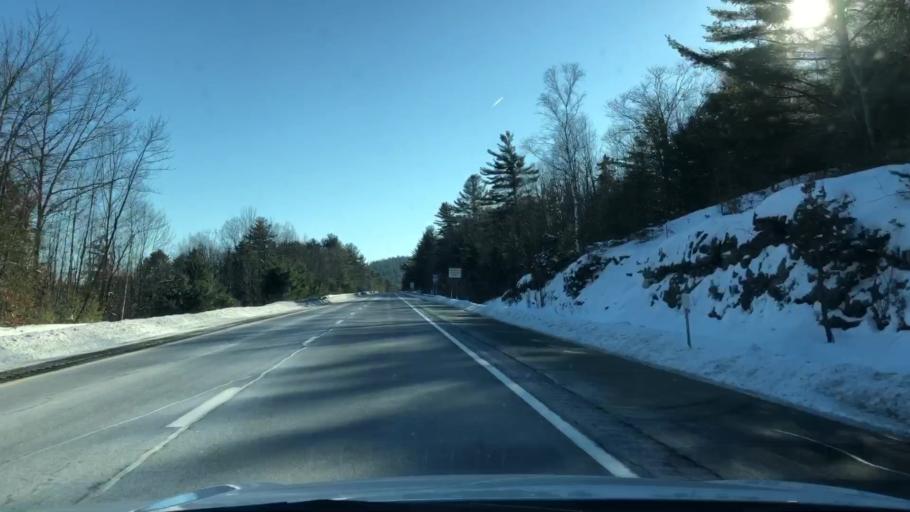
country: US
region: New York
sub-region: Warren County
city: Warrensburg
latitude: 43.7730
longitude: -73.8018
